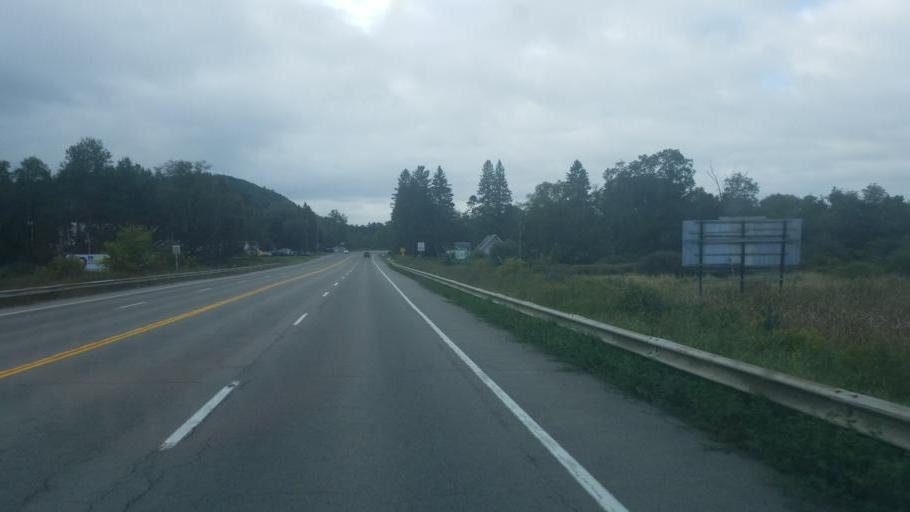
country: US
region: New York
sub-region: Cattaraugus County
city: Weston Mills
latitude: 42.1585
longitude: -78.3973
